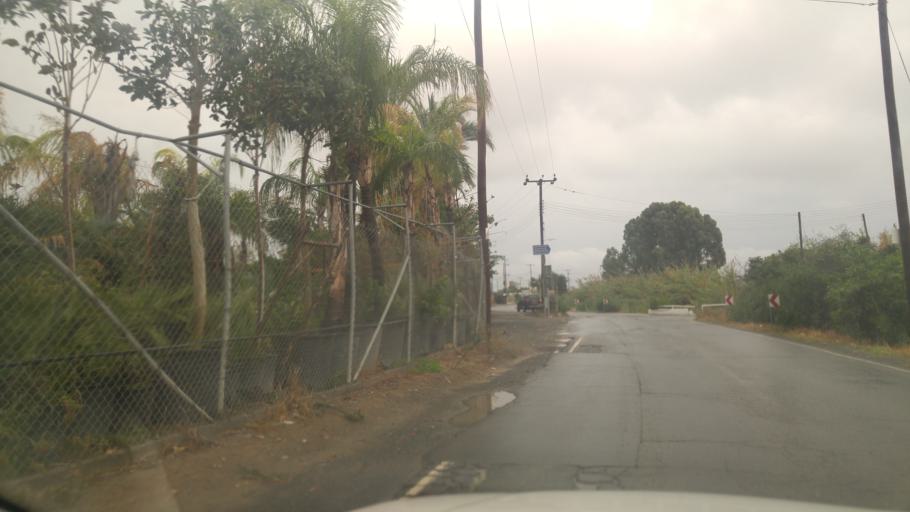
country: CY
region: Limassol
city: Mouttagiaka
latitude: 34.7125
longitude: 33.0898
